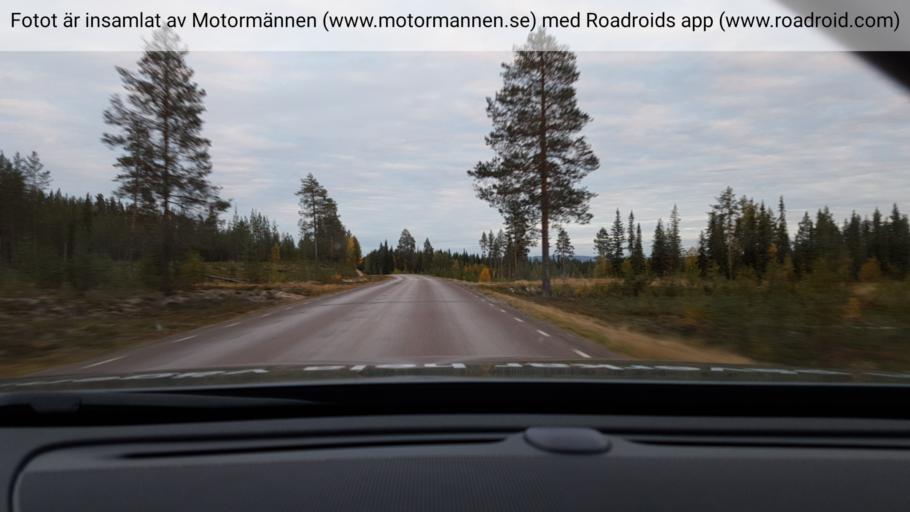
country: SE
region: Norrbotten
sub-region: Jokkmokks Kommun
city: Jokkmokk
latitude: 65.9812
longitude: 20.2072
